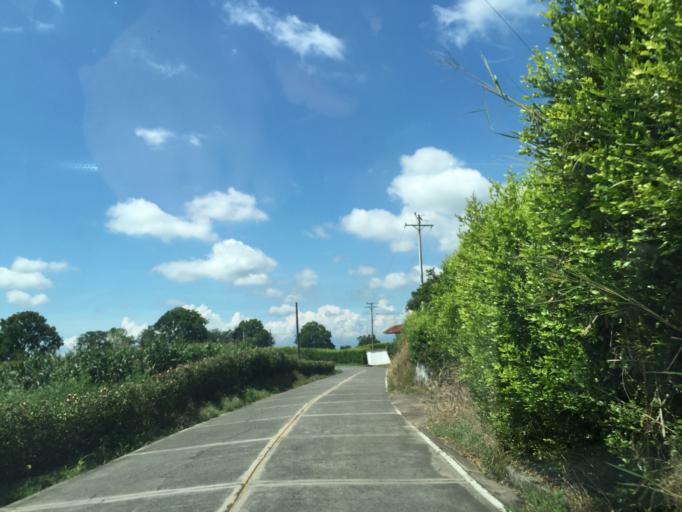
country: CO
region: Valle del Cauca
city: Ulloa
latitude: 4.6997
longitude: -75.7581
